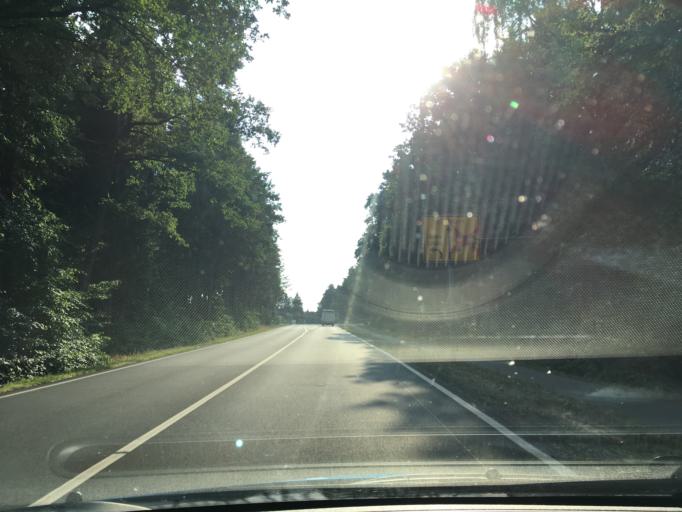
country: DE
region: Lower Saxony
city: Zernien
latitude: 53.0750
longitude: 10.9499
